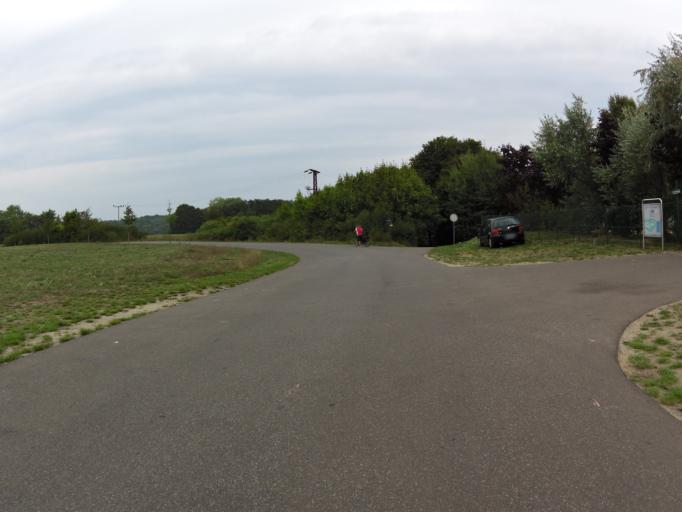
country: PL
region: West Pomeranian Voivodeship
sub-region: Swinoujscie
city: Swinoujscie
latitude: 53.8764
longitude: 14.2061
